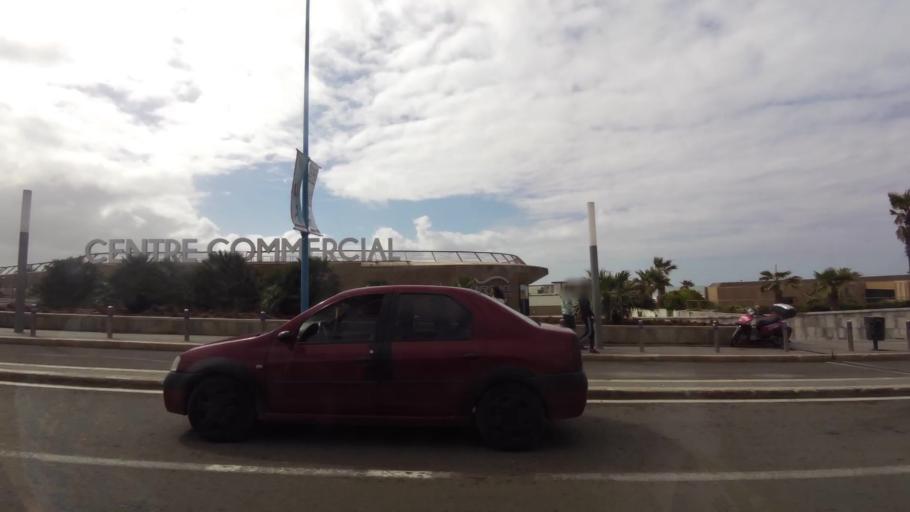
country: MA
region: Grand Casablanca
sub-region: Casablanca
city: Casablanca
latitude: 33.5984
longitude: -7.6635
